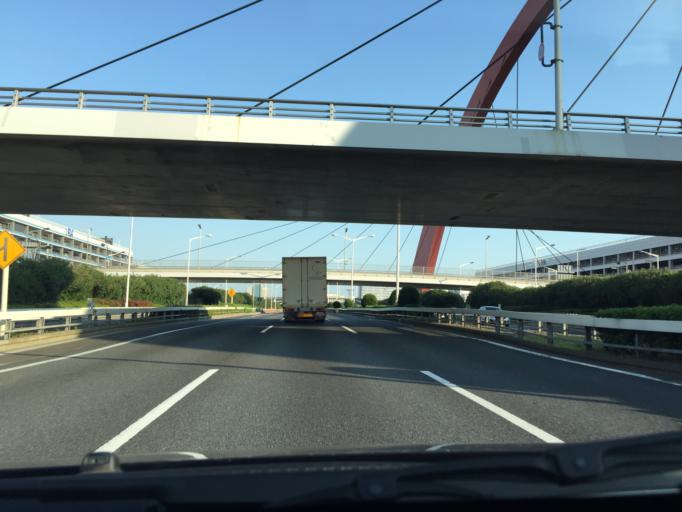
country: JP
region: Kanagawa
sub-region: Kawasaki-shi
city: Kawasaki
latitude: 35.5506
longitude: 139.7860
